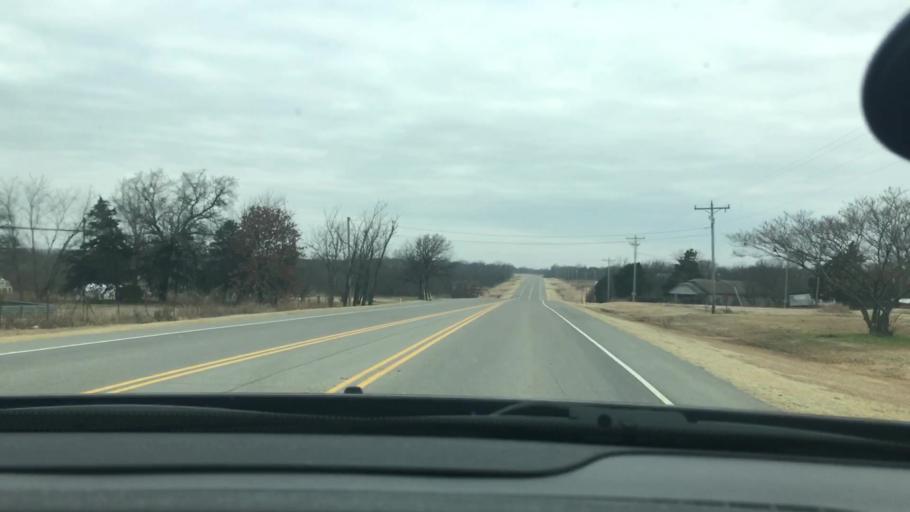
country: US
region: Oklahoma
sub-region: Carter County
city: Healdton
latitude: 34.4823
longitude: -97.4603
